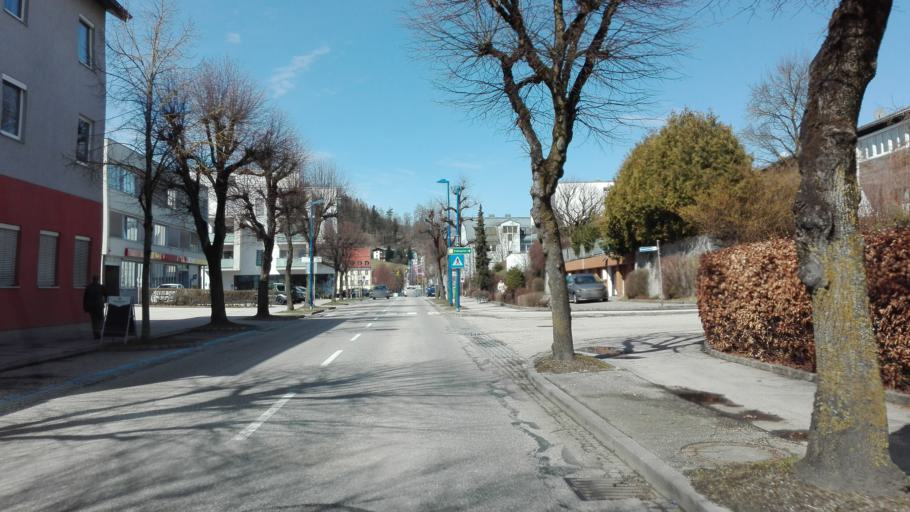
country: AT
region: Upper Austria
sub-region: Politischer Bezirk Grieskirchen
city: Bad Schallerbach
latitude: 48.2302
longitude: 13.9224
